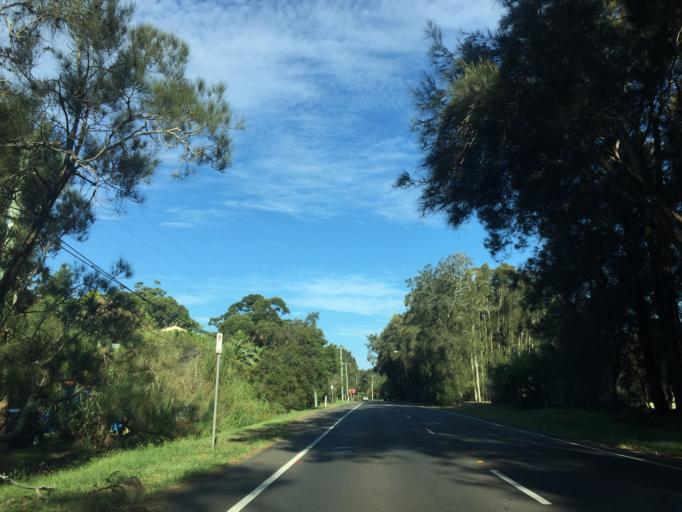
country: AU
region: New South Wales
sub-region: Pittwater
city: North Narrabeen
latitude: -33.7102
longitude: 151.2884
